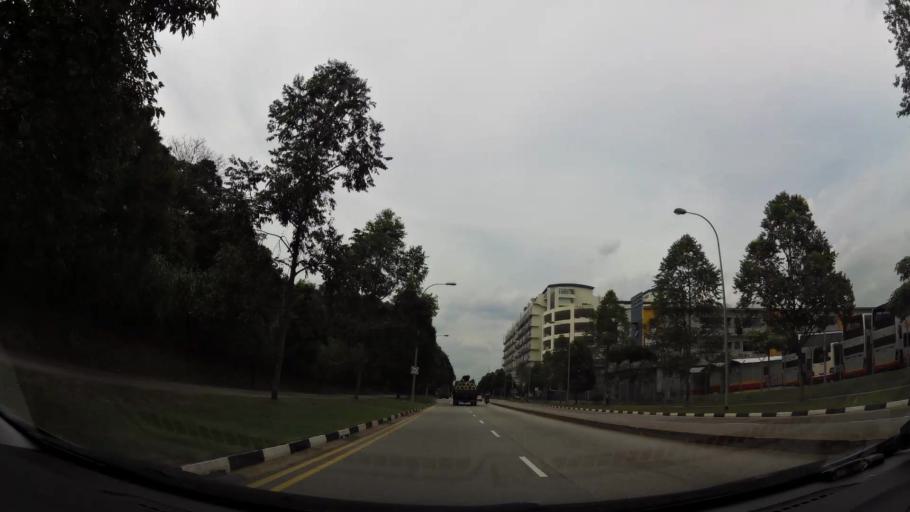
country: MY
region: Johor
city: Johor Bahru
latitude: 1.4487
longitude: 103.7914
